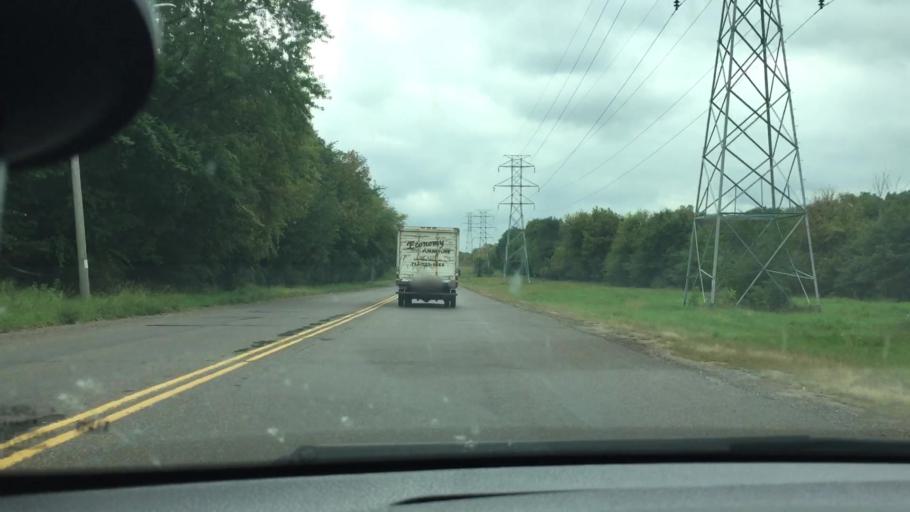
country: US
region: Wisconsin
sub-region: Chippewa County
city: Chippewa Falls
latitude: 44.9234
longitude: -91.3917
